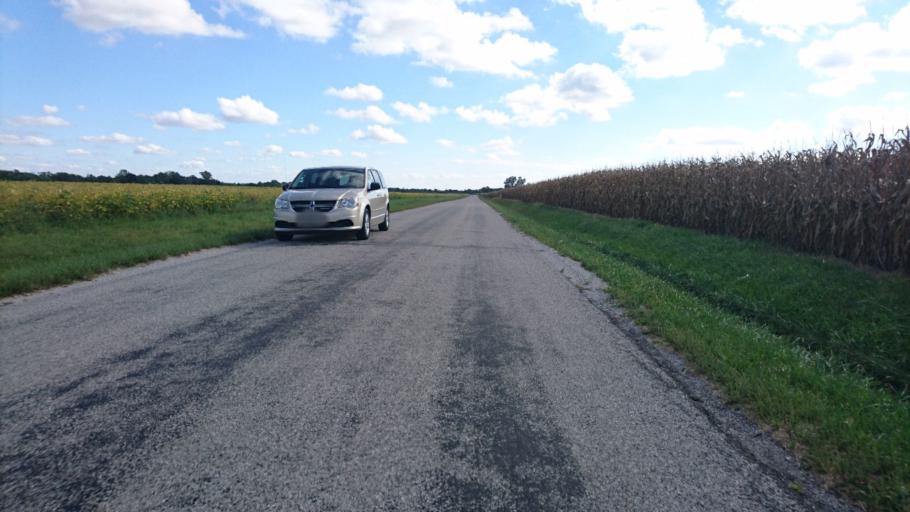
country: US
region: Illinois
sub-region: Macoupin County
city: Staunton
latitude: 39.0122
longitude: -89.7314
